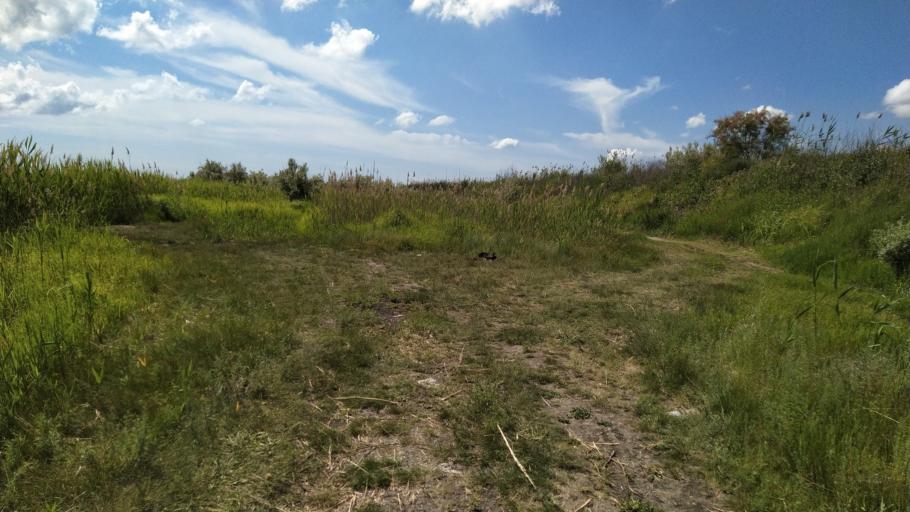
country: RU
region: Rostov
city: Bataysk
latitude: 47.1355
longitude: 39.6742
